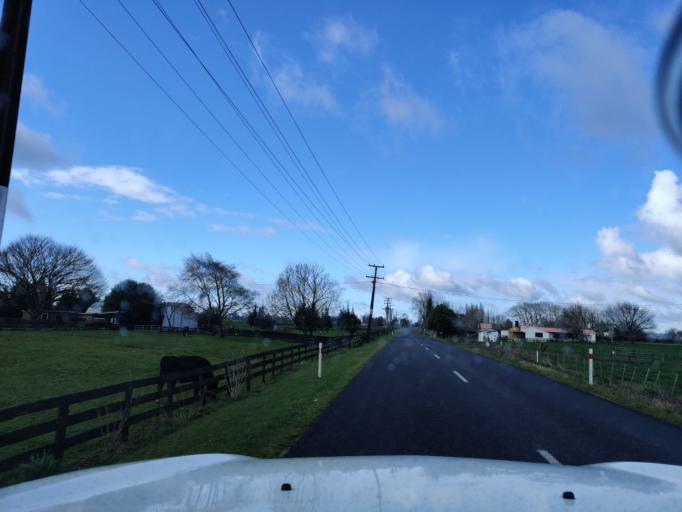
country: NZ
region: Waikato
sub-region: Waikato District
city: Ngaruawahia
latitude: -37.5728
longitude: 175.2663
